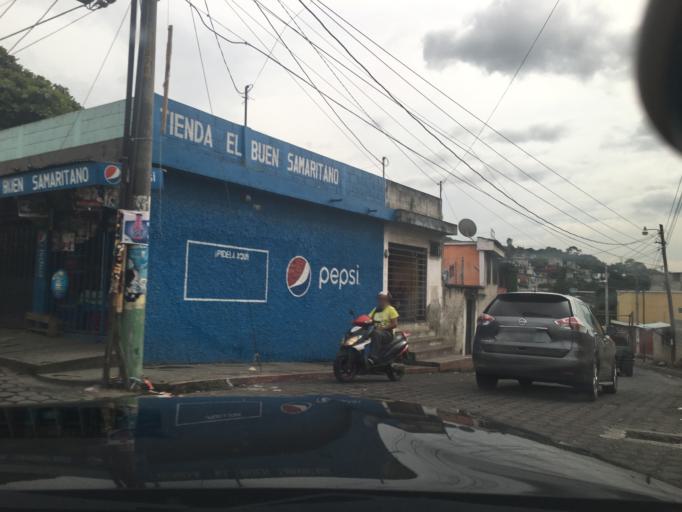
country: GT
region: Guatemala
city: Amatitlan
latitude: 14.4793
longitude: -90.6136
